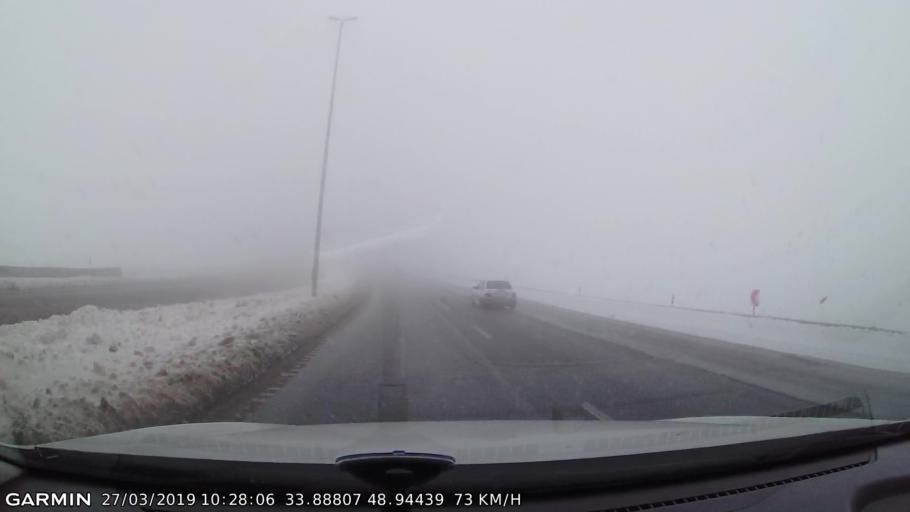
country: IR
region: Lorestan
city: Borujerd
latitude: 33.8891
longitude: 48.9489
